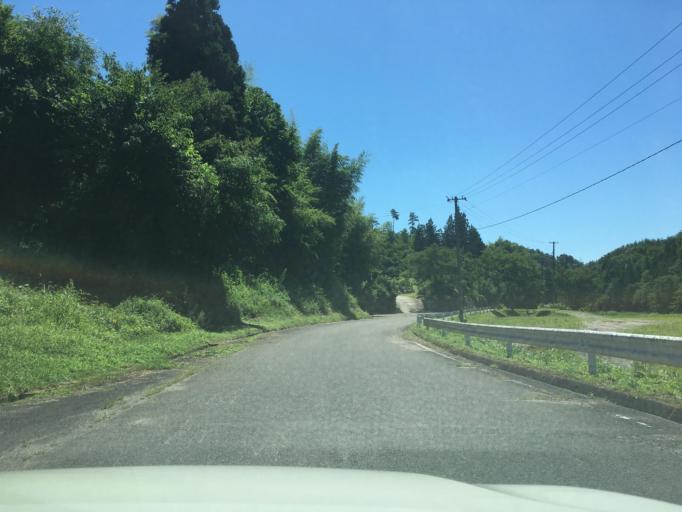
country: JP
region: Fukushima
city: Ishikawa
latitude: 37.2168
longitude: 140.5249
